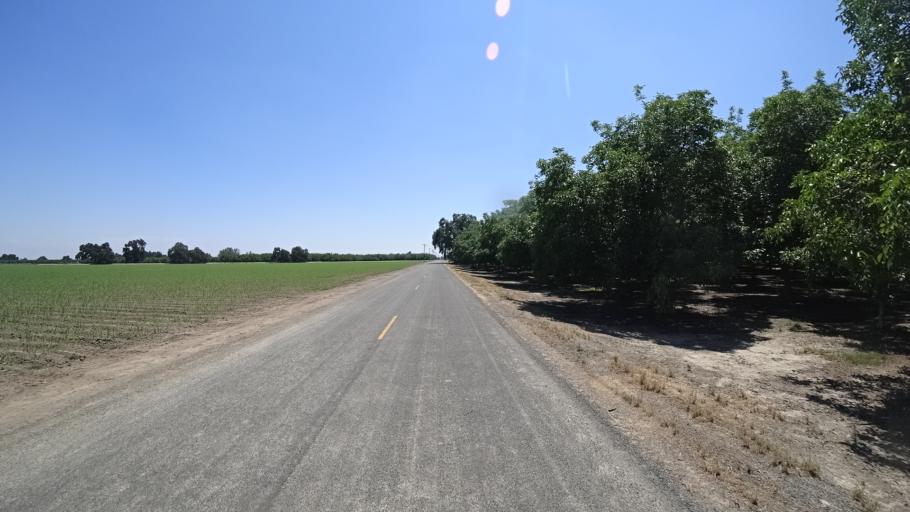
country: US
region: California
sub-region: Fresno County
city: Laton
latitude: 36.4186
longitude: -119.6952
